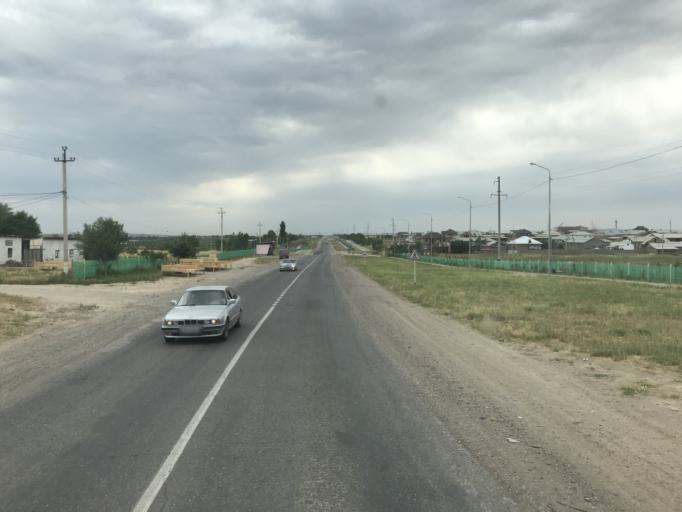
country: KZ
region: Ongtustik Qazaqstan
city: Saryaghash
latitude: 41.4221
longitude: 69.0920
